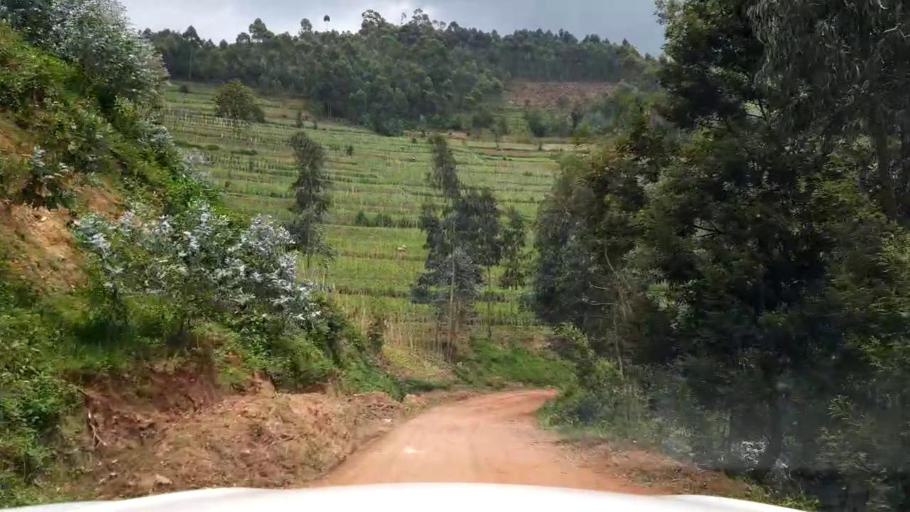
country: RW
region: Northern Province
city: Byumba
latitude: -1.4821
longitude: 29.9213
